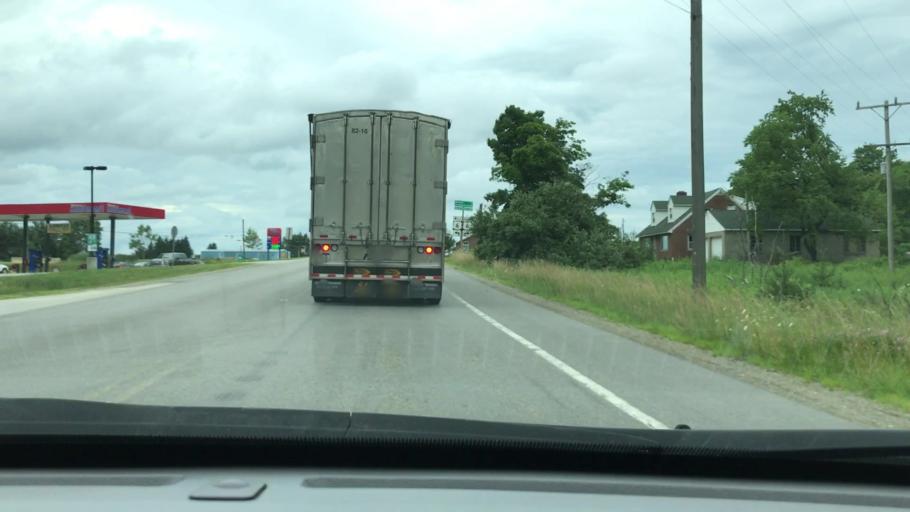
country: US
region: Pennsylvania
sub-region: McKean County
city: Kane
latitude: 41.7067
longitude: -78.6936
